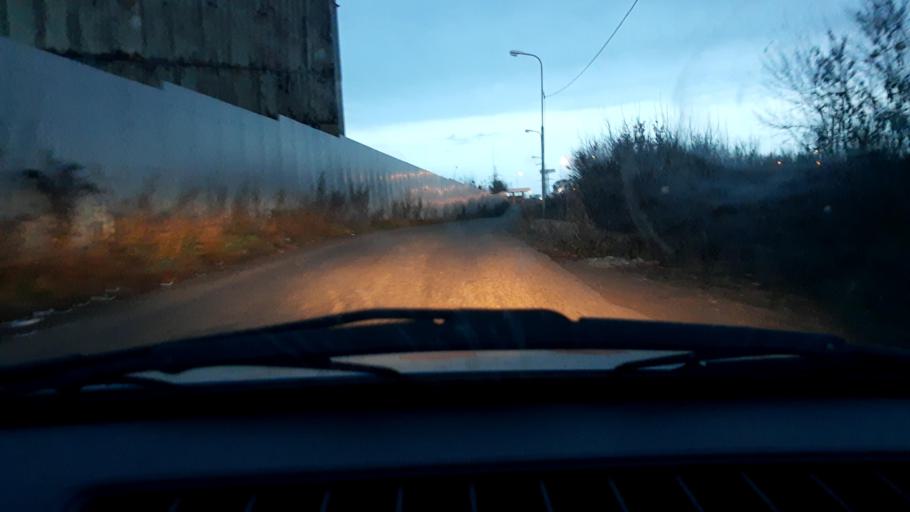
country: RU
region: Bashkortostan
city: Avdon
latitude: 54.6742
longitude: 55.8063
